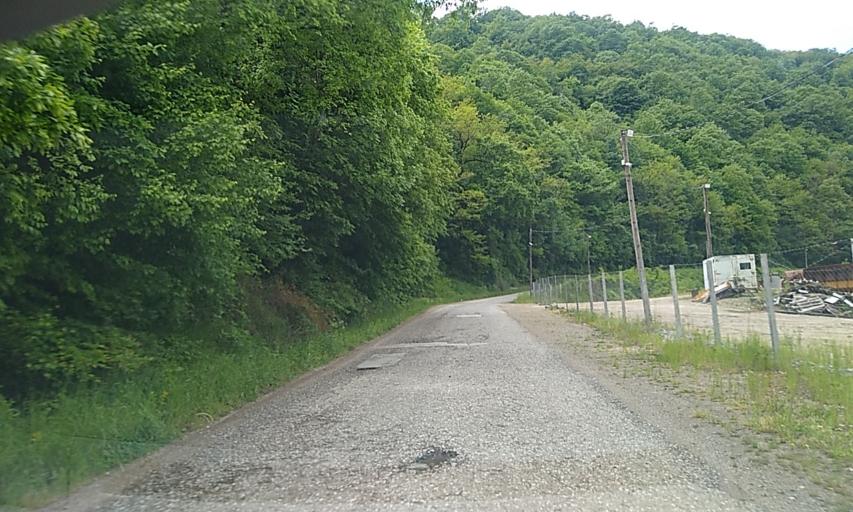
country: RS
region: Central Serbia
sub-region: Pcinjski Okrug
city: Vladicin Han
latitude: 42.7341
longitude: 22.0574
